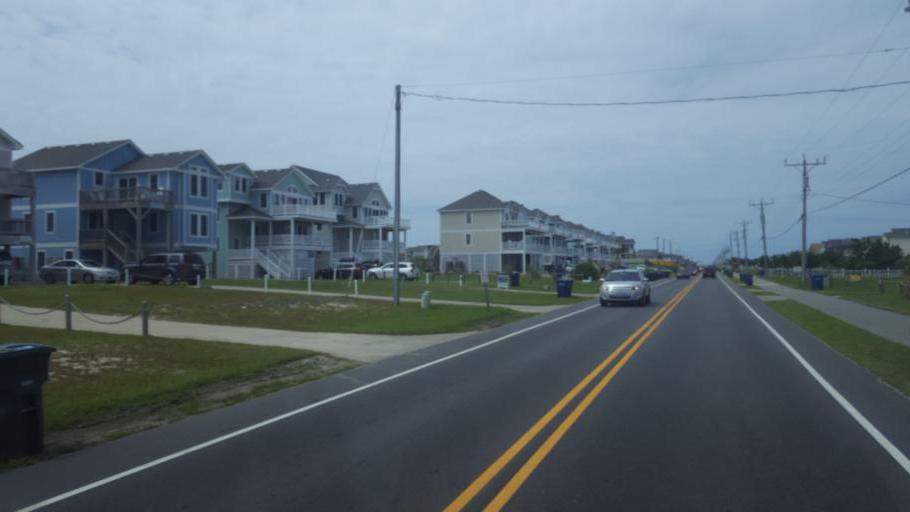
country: US
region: North Carolina
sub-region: Dare County
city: Nags Head
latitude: 35.9658
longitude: -75.6289
